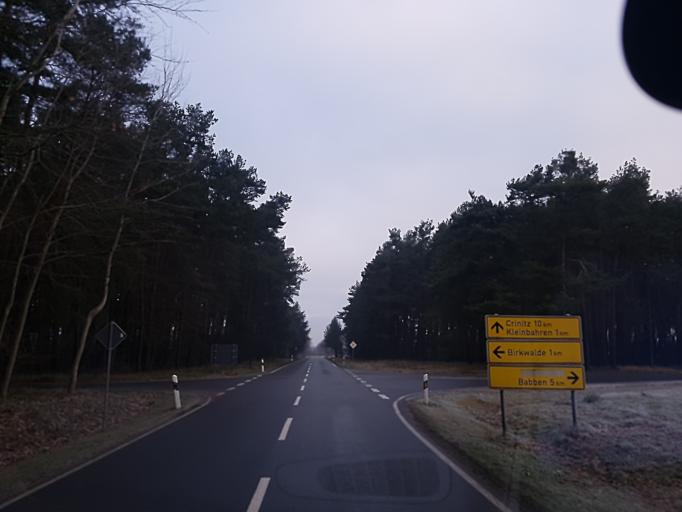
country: DE
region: Brandenburg
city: Crinitz
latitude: 51.6923
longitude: 13.7237
